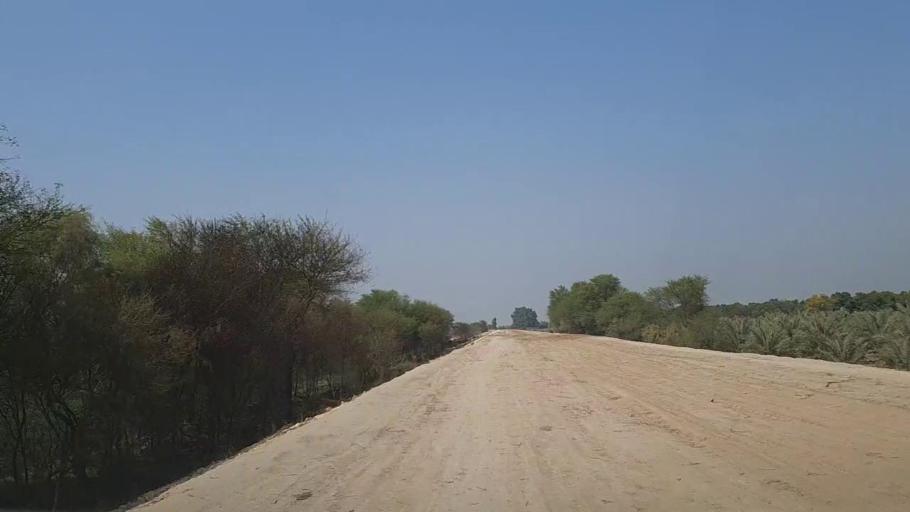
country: PK
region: Sindh
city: Moro
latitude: 26.8156
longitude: 67.9547
